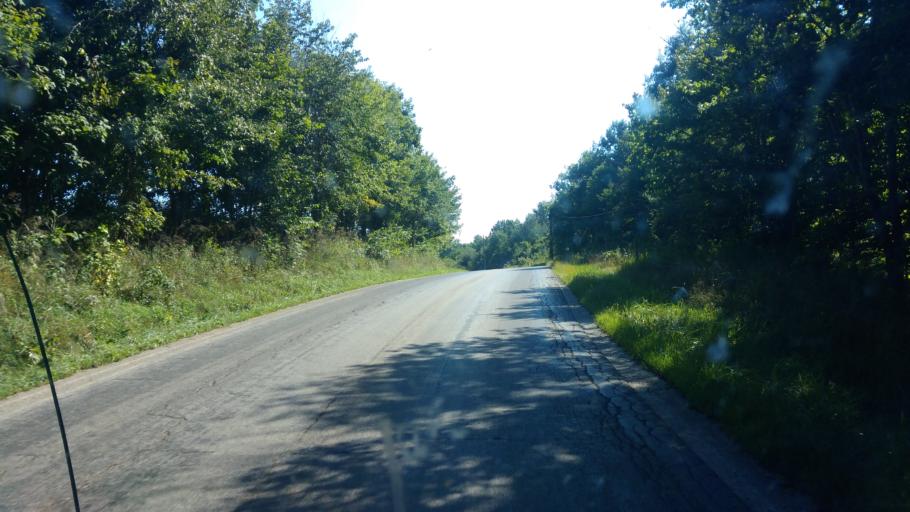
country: US
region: Ohio
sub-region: Ashland County
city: Ashland
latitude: 40.9105
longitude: -82.4355
